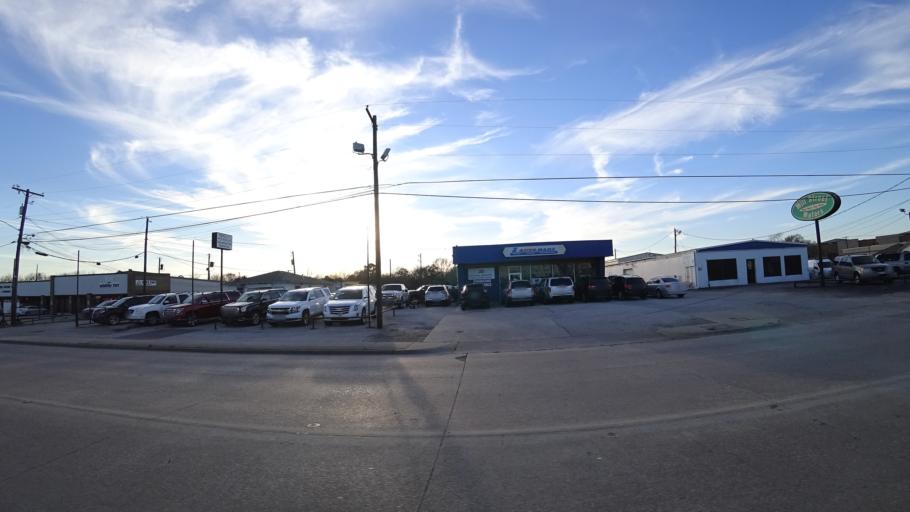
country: US
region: Texas
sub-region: Denton County
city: Lewisville
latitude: 33.0389
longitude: -96.9928
